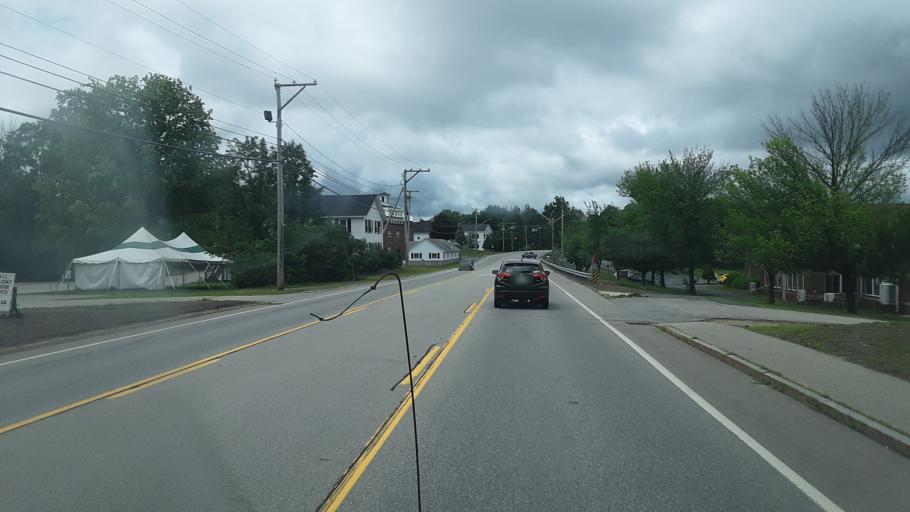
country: US
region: New Hampshire
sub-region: Rockingham County
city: Northwood
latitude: 43.2176
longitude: -71.2086
